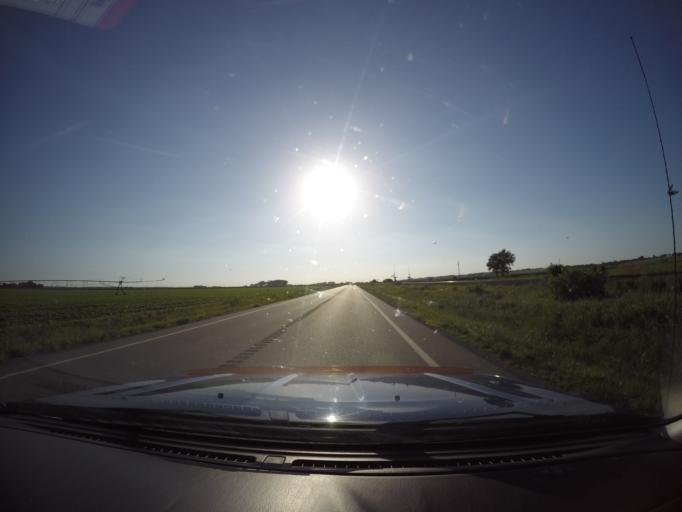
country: US
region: Kansas
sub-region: Shawnee County
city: Silver Lake
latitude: 39.1081
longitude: -95.8712
